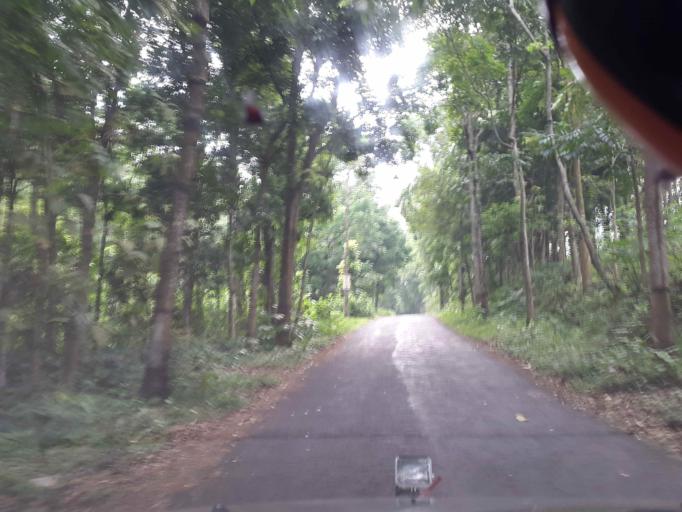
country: ID
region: East Java
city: Madiun
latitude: -7.6796
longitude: 111.2724
